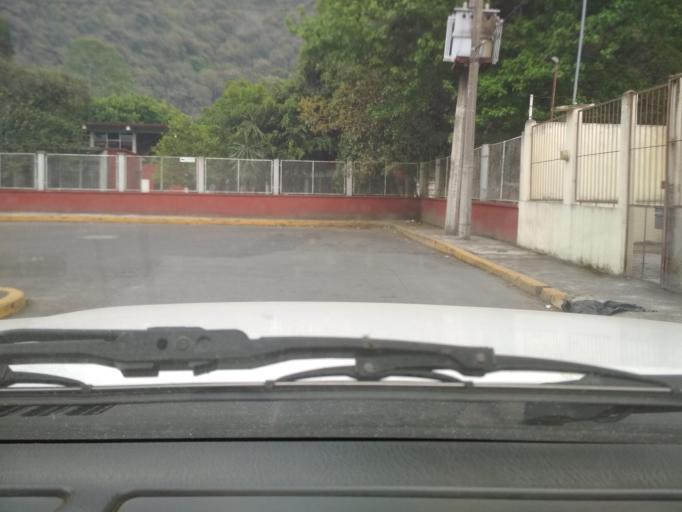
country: MX
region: Veracruz
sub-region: Mariano Escobedo
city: Palmira
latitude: 18.8727
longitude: -97.0991
